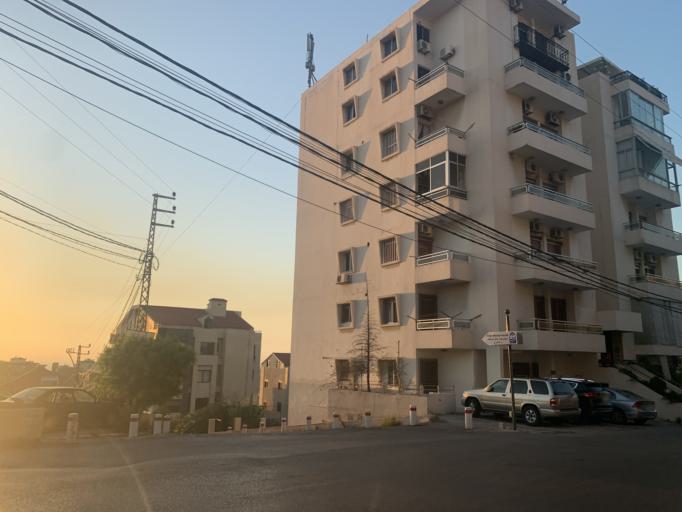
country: LB
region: Mont-Liban
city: Djounie
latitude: 33.9718
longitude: 35.6265
